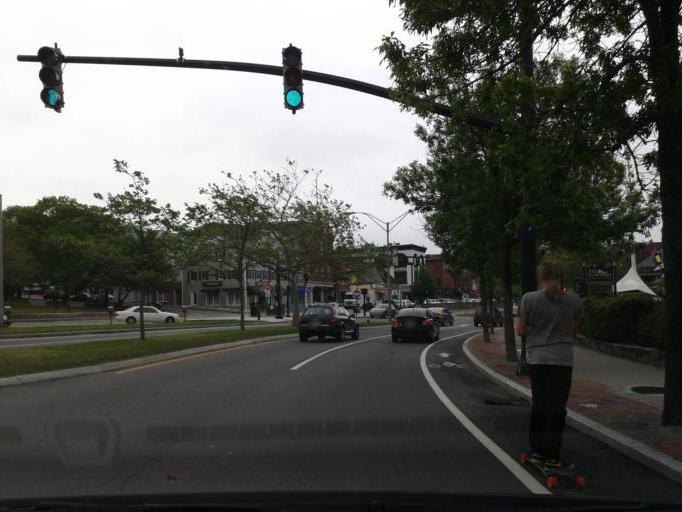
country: US
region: Rhode Island
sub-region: Newport County
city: Newport
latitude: 41.4876
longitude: -71.3156
